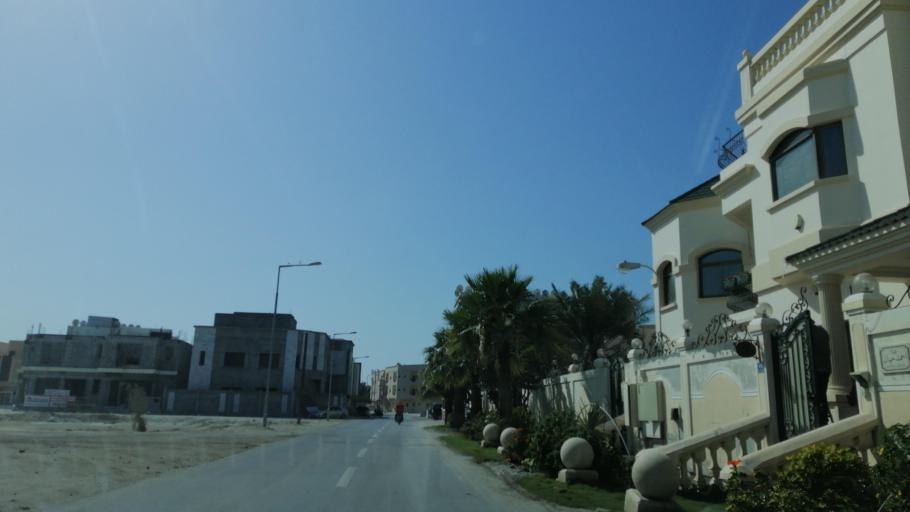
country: BH
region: Muharraq
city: Al Hadd
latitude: 26.2538
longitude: 50.6370
